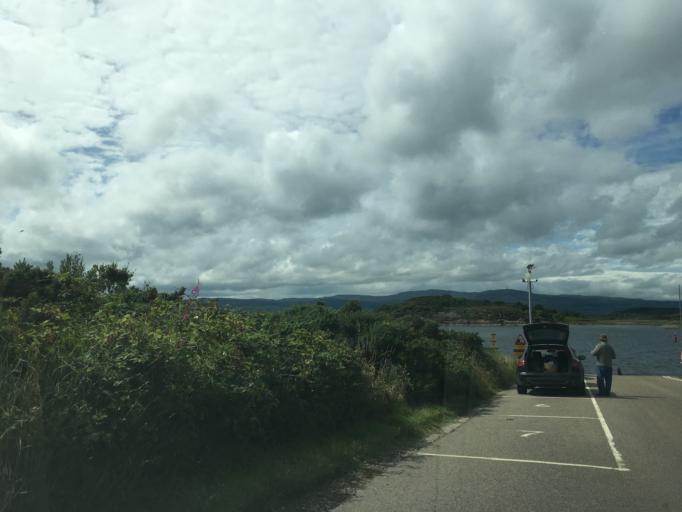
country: GB
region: Scotland
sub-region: Argyll and Bute
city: Tarbert
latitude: 55.8763
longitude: -5.3160
